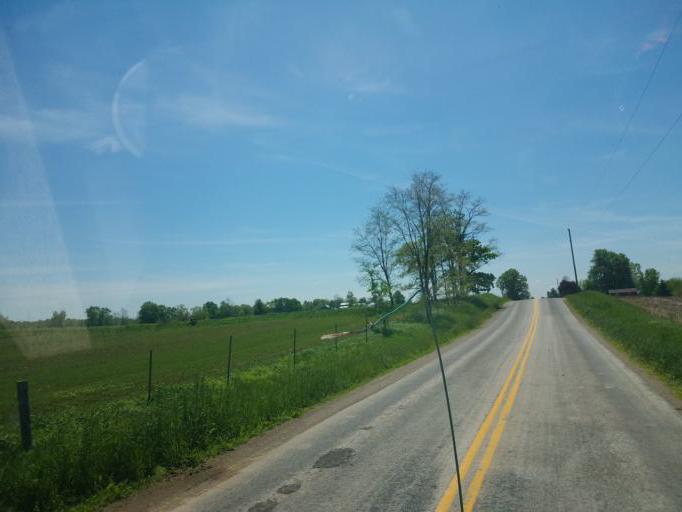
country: US
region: Ohio
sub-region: Ashland County
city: Ashland
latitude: 40.9527
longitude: -82.2437
